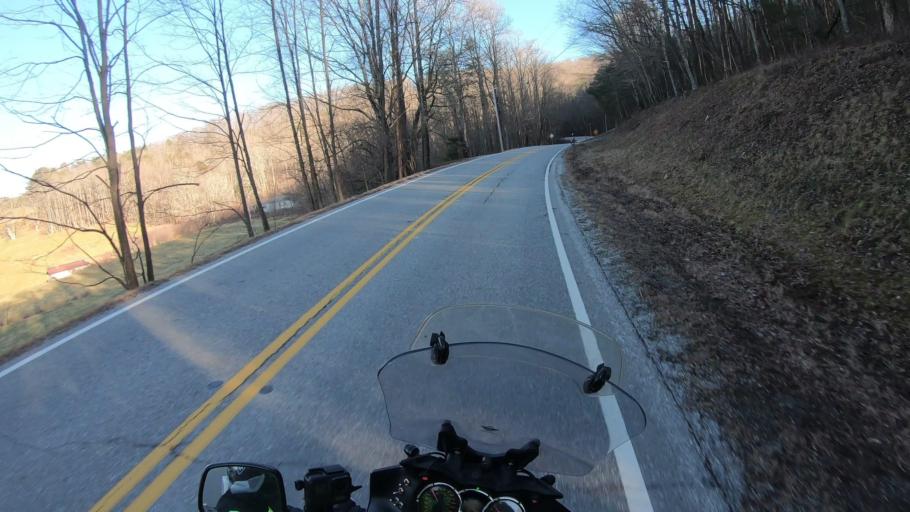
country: US
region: Georgia
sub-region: Lumpkin County
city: Dahlonega
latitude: 34.6906
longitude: -84.0172
